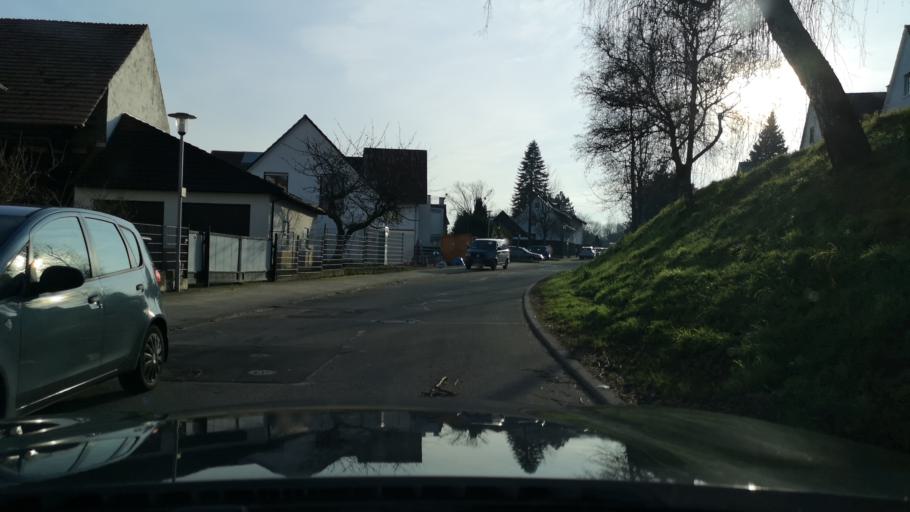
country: DE
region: Baden-Wuerttemberg
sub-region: Karlsruhe Region
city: Ettlingen
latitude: 48.9540
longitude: 8.4689
